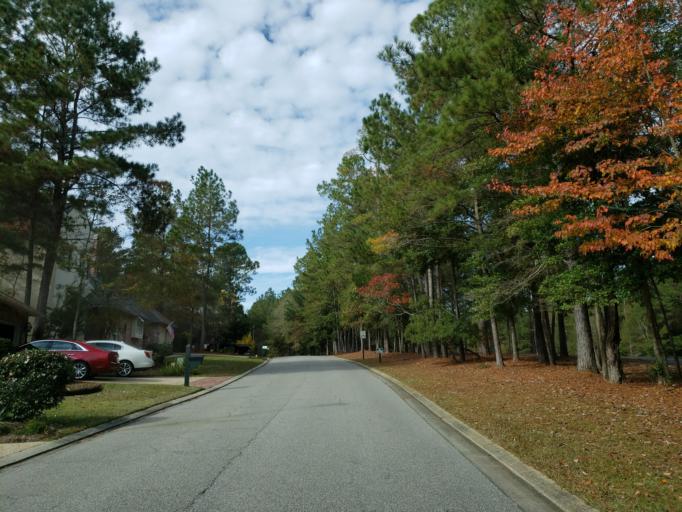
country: US
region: Mississippi
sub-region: Lamar County
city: West Hattiesburg
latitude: 31.3177
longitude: -89.4706
